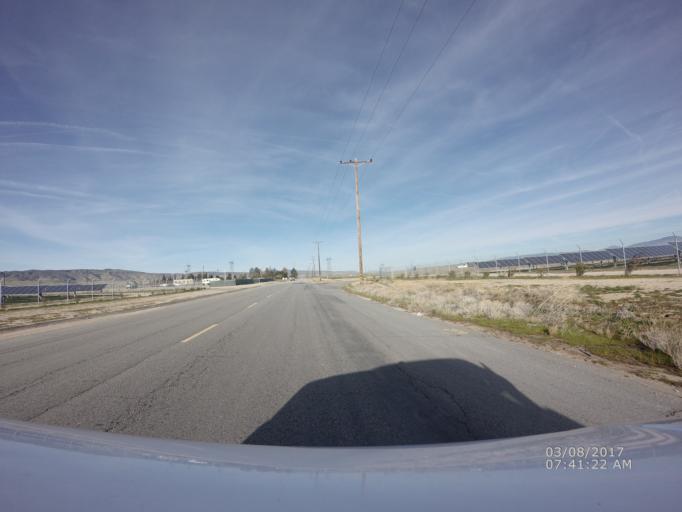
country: US
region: California
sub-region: Los Angeles County
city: Leona Valley
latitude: 34.7038
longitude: -118.3060
